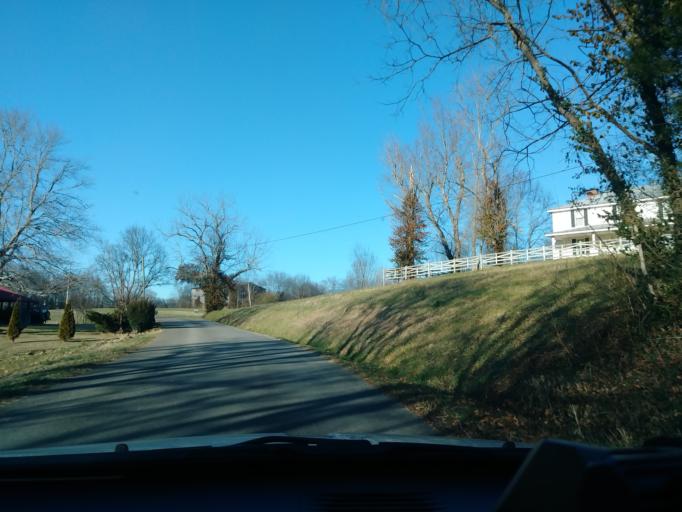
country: US
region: Tennessee
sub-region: Greene County
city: Greeneville
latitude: 36.0730
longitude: -82.9019
